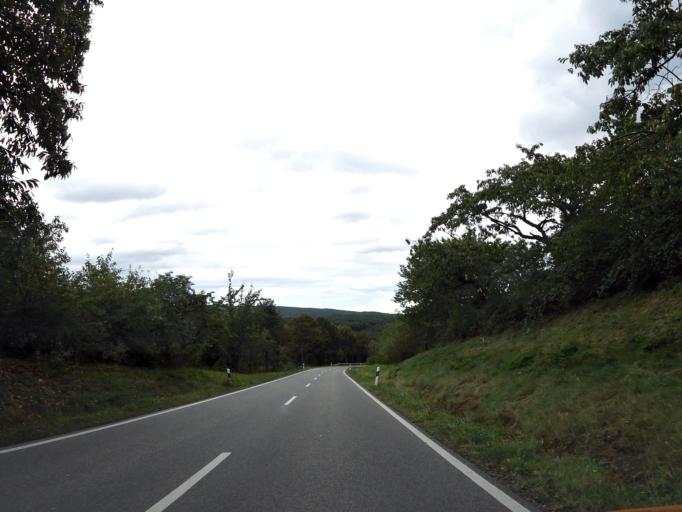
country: DE
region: Rheinland-Pfalz
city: Dannenfels
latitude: 49.6310
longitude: 7.9463
